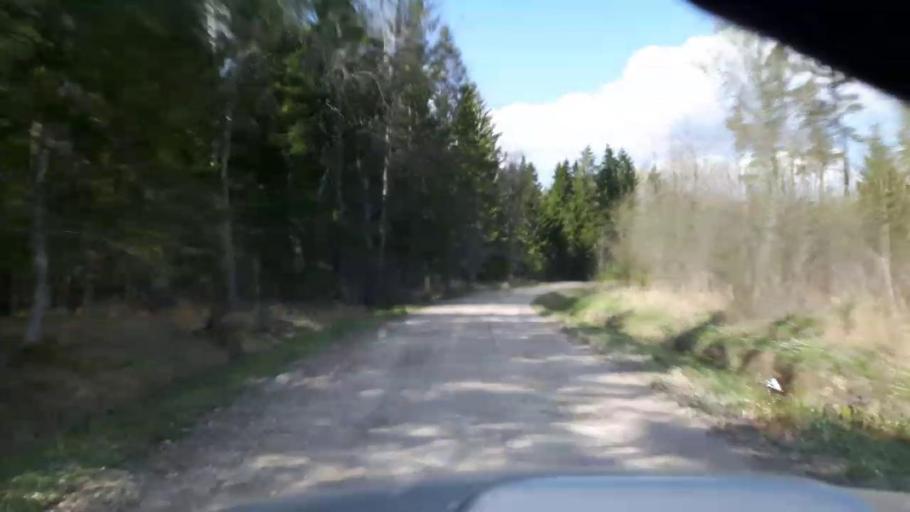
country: EE
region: Paernumaa
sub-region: Tootsi vald
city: Tootsi
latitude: 58.4547
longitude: 24.8878
